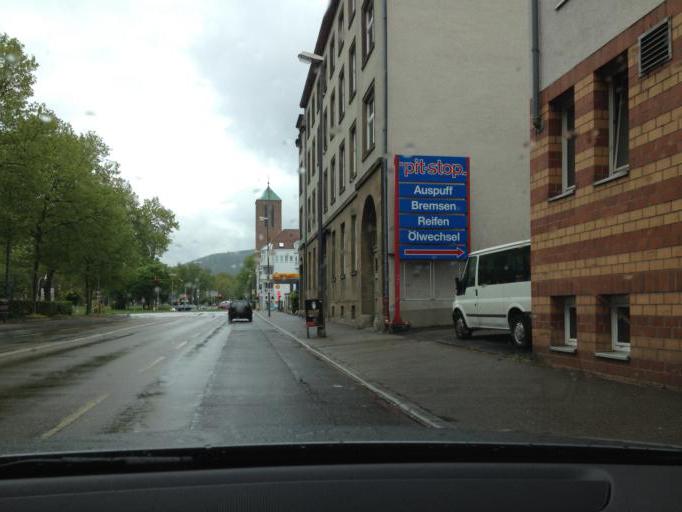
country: DE
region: Baden-Wuerttemberg
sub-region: Karlsruhe Region
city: Heidelberg
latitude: 49.4088
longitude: 8.6727
